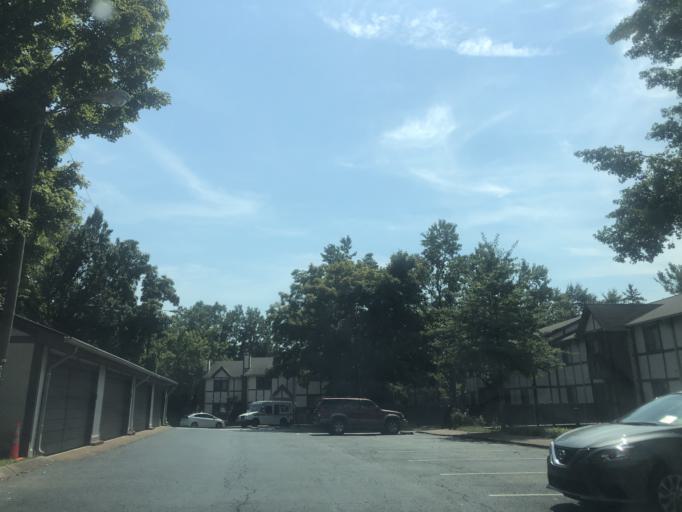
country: US
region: Tennessee
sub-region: Williamson County
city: Brentwood
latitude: 36.0558
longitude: -86.7418
